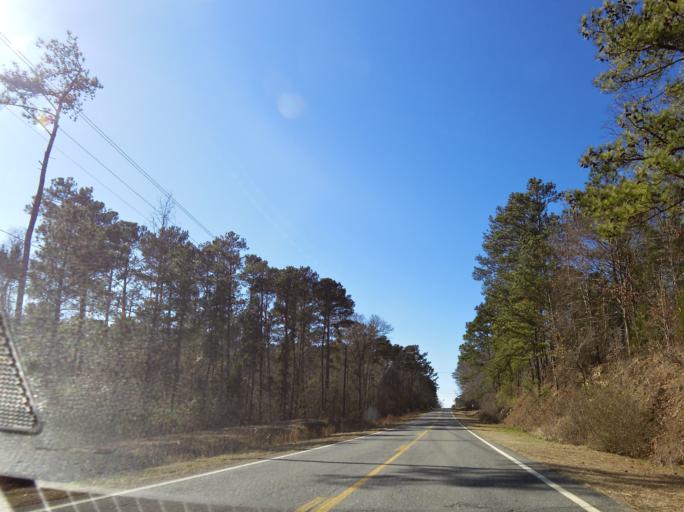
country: US
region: Georgia
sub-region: Bibb County
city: West Point
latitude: 32.8314
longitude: -83.7841
